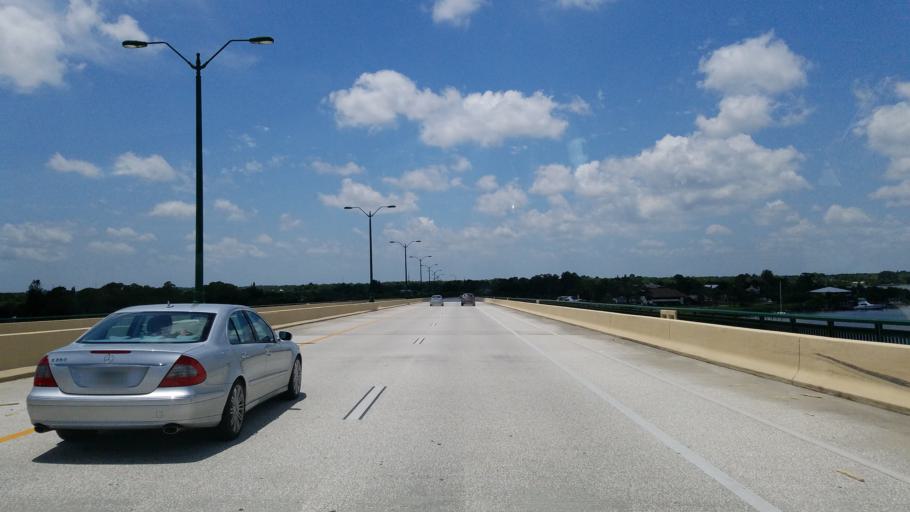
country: US
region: Florida
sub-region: Martin County
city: Palm City
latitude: 27.1600
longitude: -80.2548
